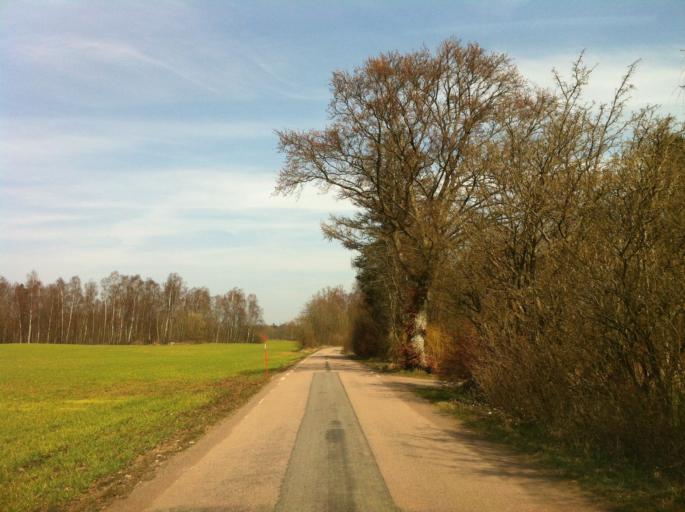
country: SE
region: Skane
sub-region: Klippans Kommun
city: Ljungbyhed
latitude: 55.9924
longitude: 13.2356
